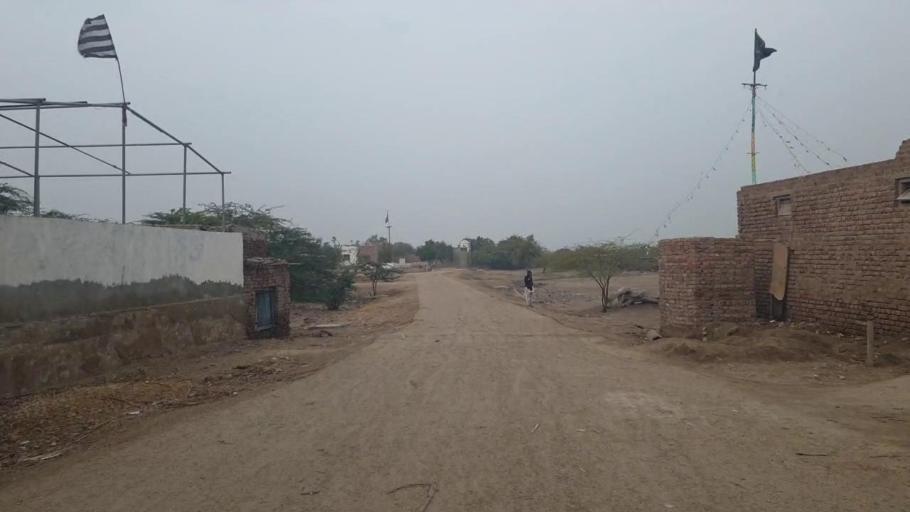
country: PK
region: Sindh
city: Berani
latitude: 25.8099
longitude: 68.7365
